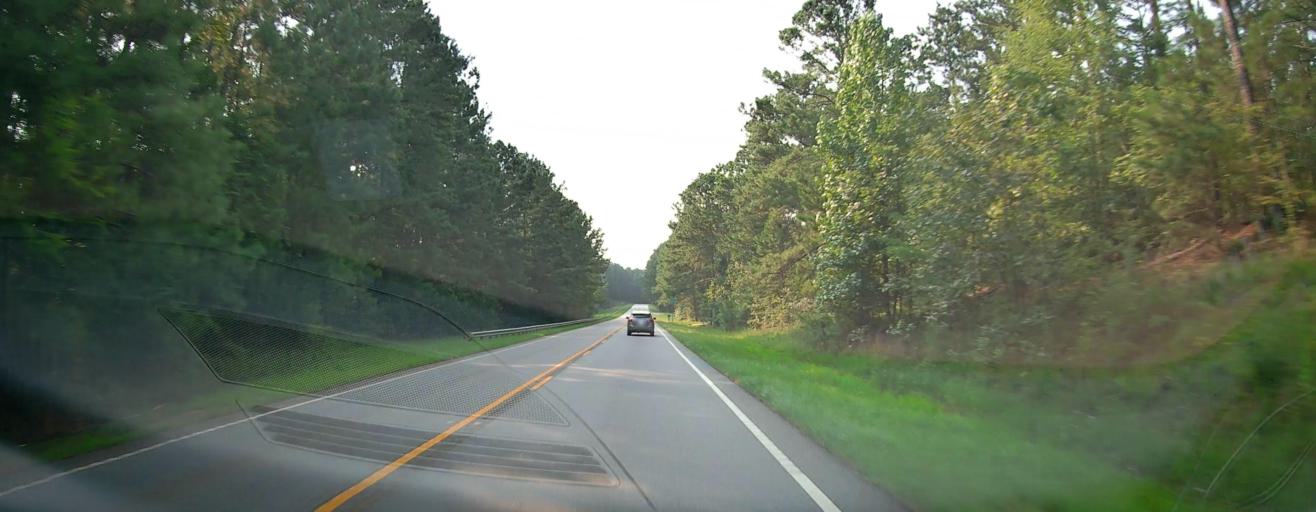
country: US
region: Georgia
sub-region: Monroe County
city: Forsyth
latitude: 33.0358
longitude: -83.7507
